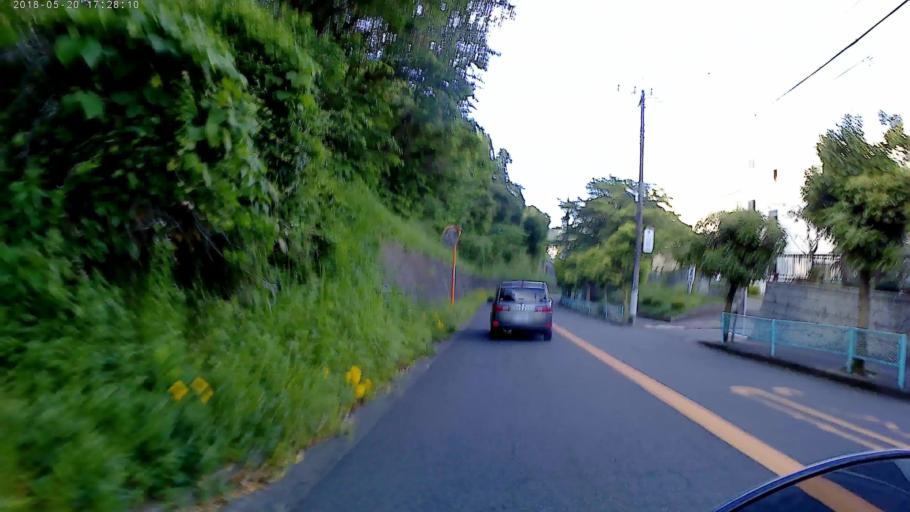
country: JP
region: Kanagawa
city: Ninomiya
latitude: 35.3114
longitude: 139.2396
